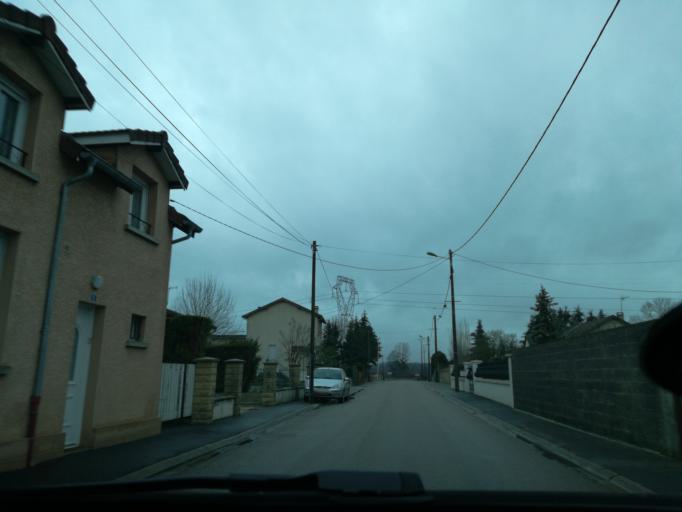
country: FR
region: Lorraine
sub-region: Departement de la Meuse
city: Revigny-sur-Ornain
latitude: 48.8243
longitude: 5.0440
